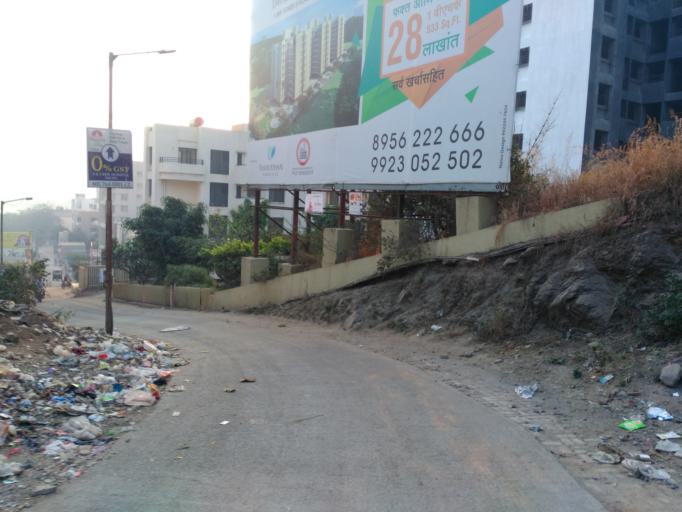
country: IN
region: Maharashtra
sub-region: Pune Division
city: Pune
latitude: 18.4468
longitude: 73.8803
